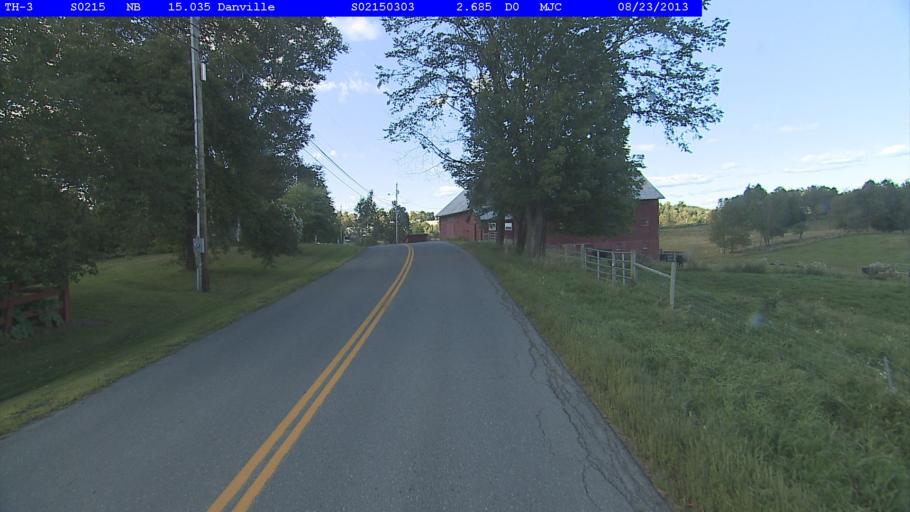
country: US
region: Vermont
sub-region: Caledonia County
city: Saint Johnsbury
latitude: 44.4033
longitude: -72.1411
